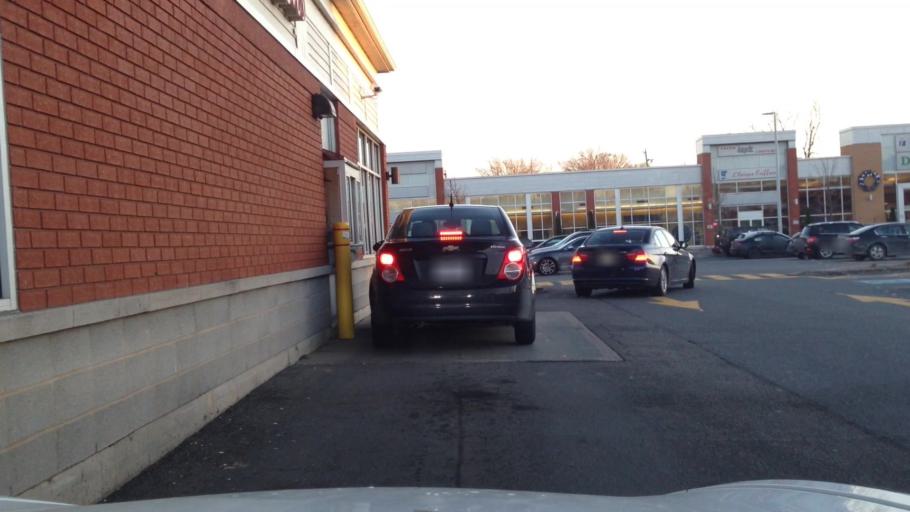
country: CA
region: Quebec
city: Beaconsfield
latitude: 45.4333
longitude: -73.8484
